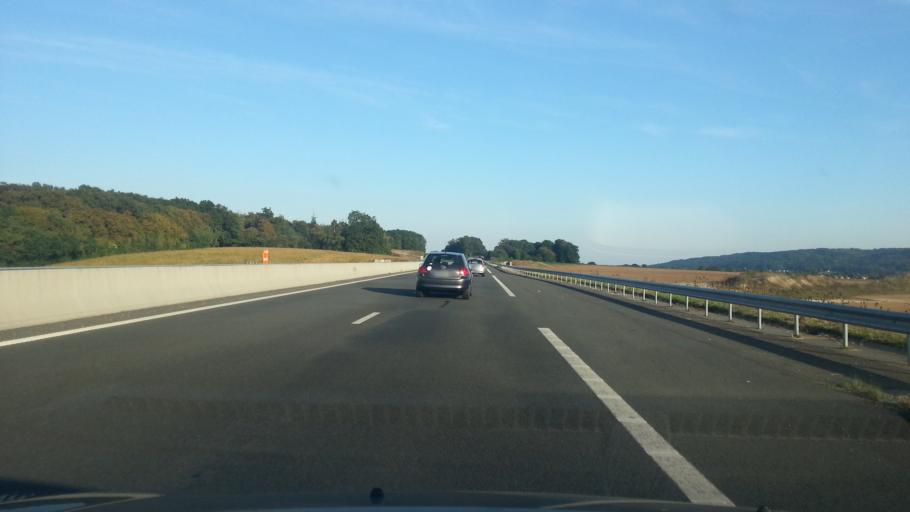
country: FR
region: Picardie
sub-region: Departement de l'Oise
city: Breuil-le-Sec
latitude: 49.3857
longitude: 2.4701
